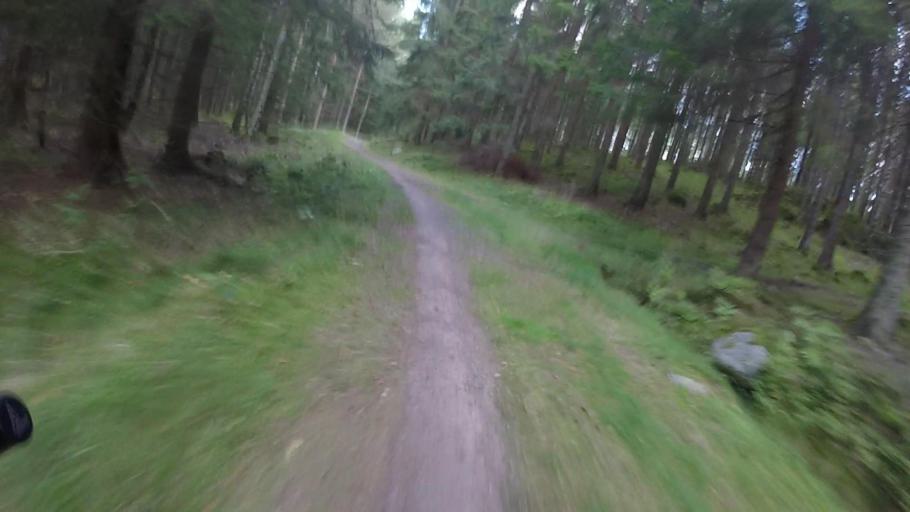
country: SE
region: Vaestra Goetaland
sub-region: Trollhattan
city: Trollhattan
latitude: 58.2563
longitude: 12.2388
